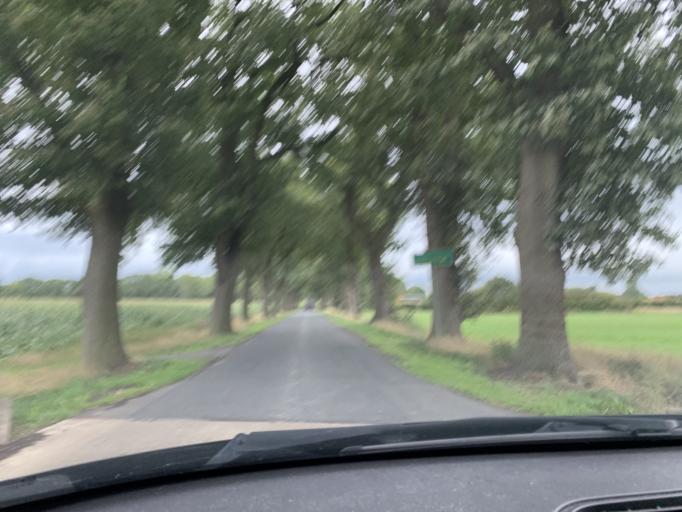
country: DE
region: Lower Saxony
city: Westerstede
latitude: 53.2770
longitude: 7.8886
